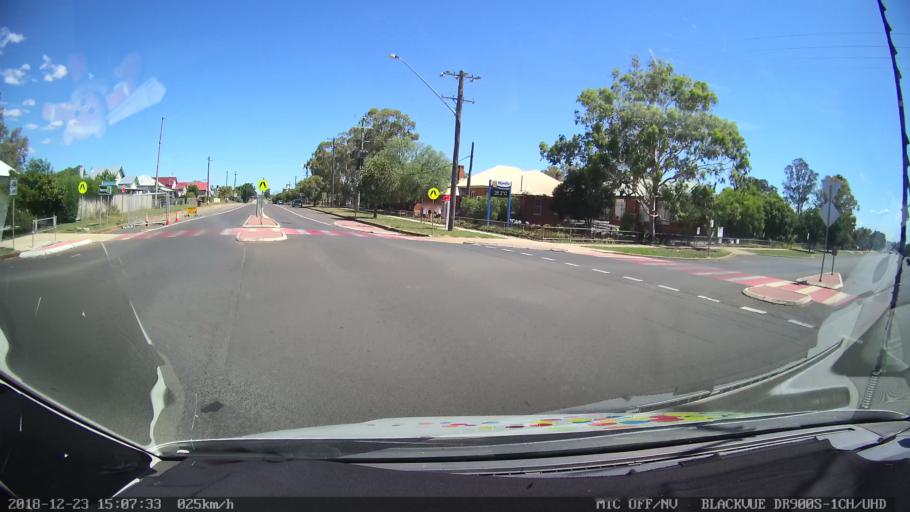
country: AU
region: New South Wales
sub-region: Tamworth Municipality
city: Manilla
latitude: -30.7484
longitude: 150.7245
